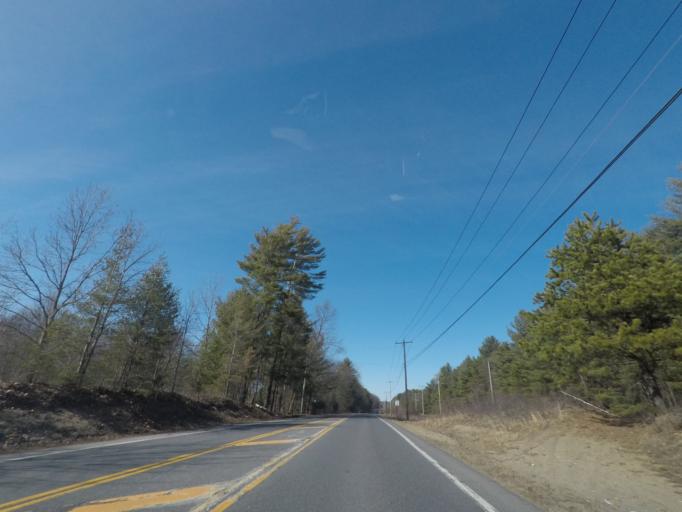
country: US
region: New York
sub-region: Saratoga County
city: Milton
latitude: 43.0501
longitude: -73.8506
